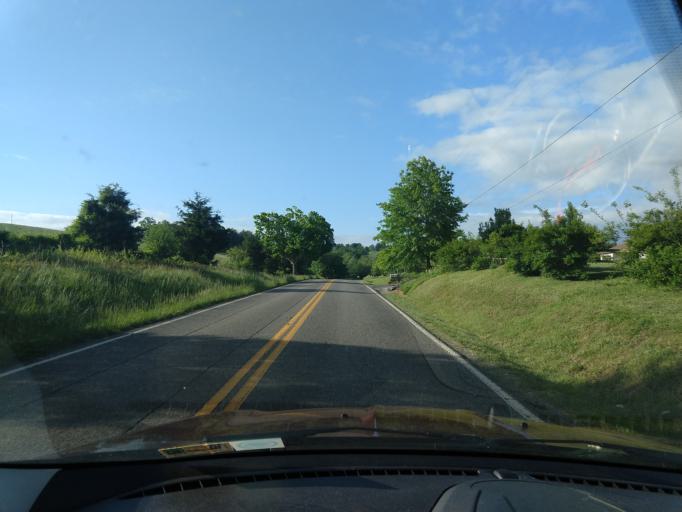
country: US
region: Virginia
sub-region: Wythe County
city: Wytheville
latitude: 36.8463
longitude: -80.9720
